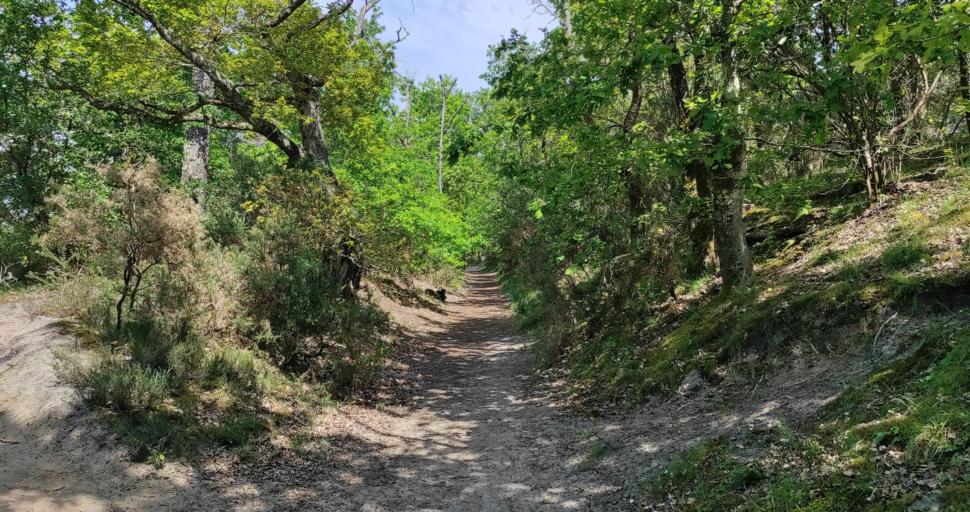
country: FR
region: Aquitaine
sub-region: Departement de la Gironde
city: Andernos-les-Bains
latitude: 44.7529
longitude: -1.1192
